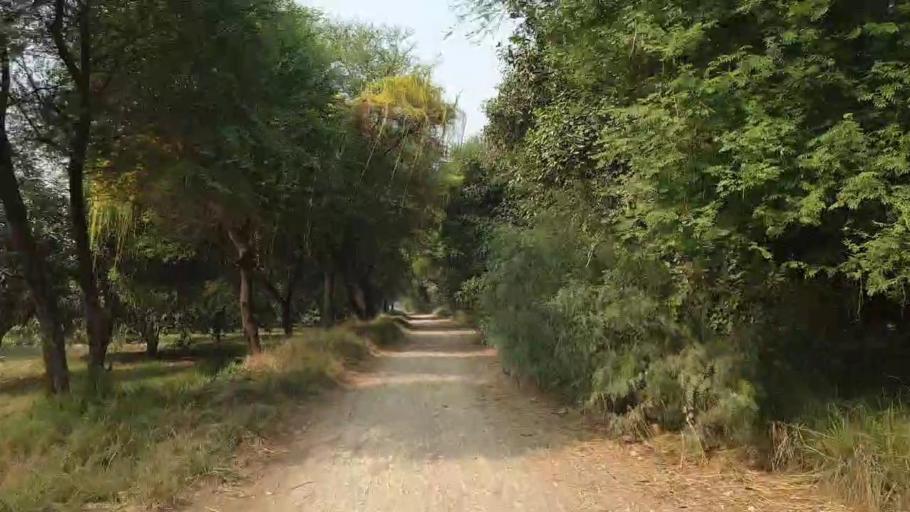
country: PK
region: Sindh
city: Tando Muhammad Khan
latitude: 25.2105
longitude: 68.5587
